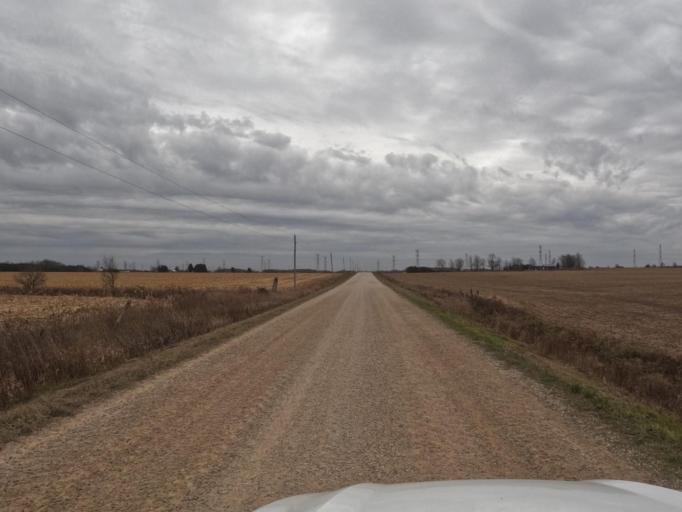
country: CA
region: Ontario
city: Shelburne
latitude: 43.9990
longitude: -80.3867
